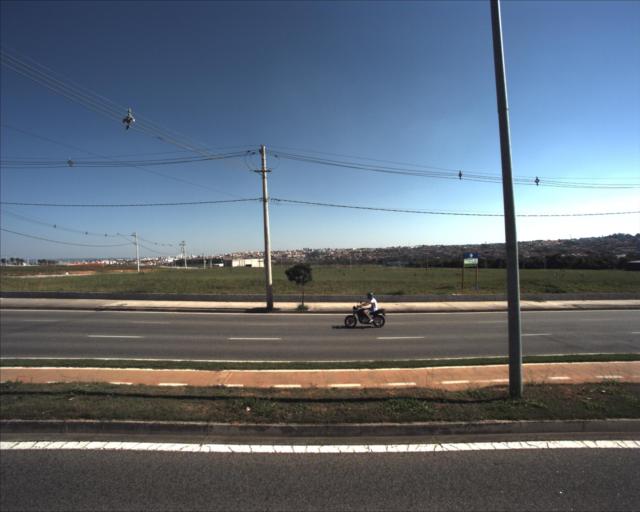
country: BR
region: Sao Paulo
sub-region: Sorocaba
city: Sorocaba
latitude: -23.4529
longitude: -47.4555
